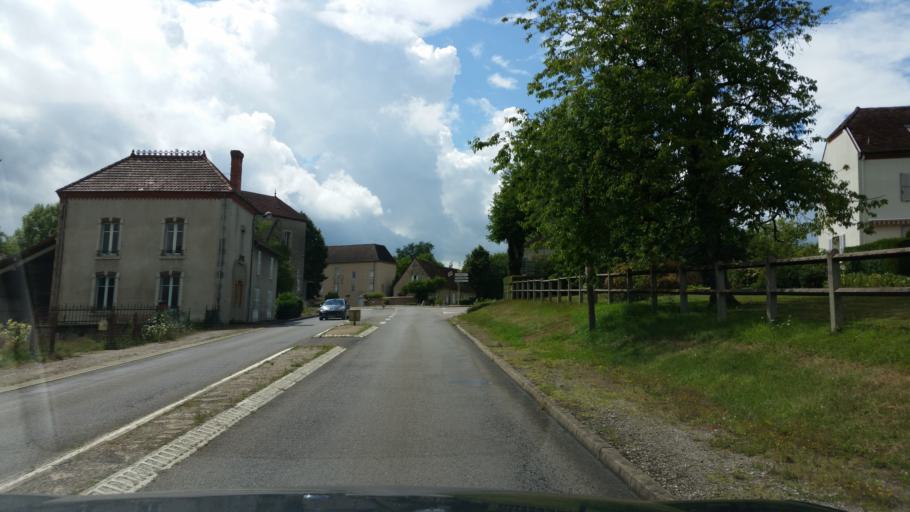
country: FR
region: Franche-Comte
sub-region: Departement du Jura
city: Bletterans
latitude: 46.6715
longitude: 5.3931
